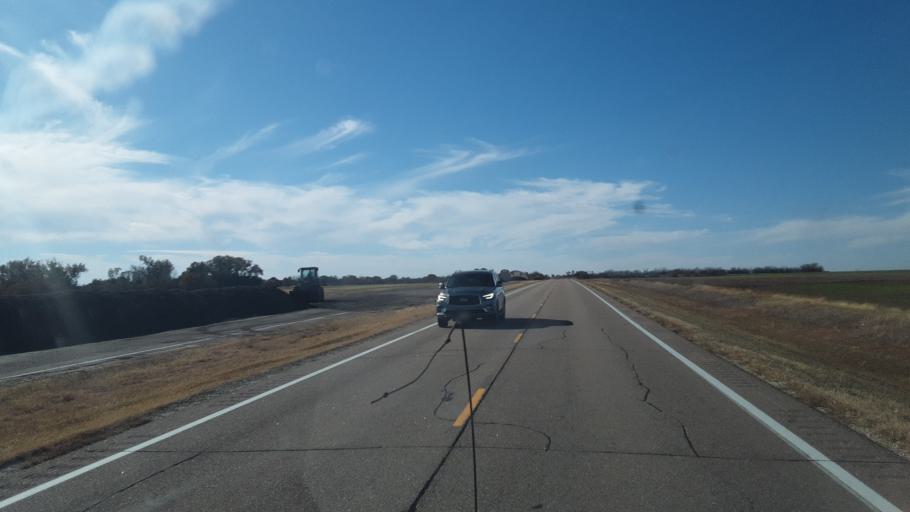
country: US
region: Kansas
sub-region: Pawnee County
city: Larned
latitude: 38.1895
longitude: -99.2920
